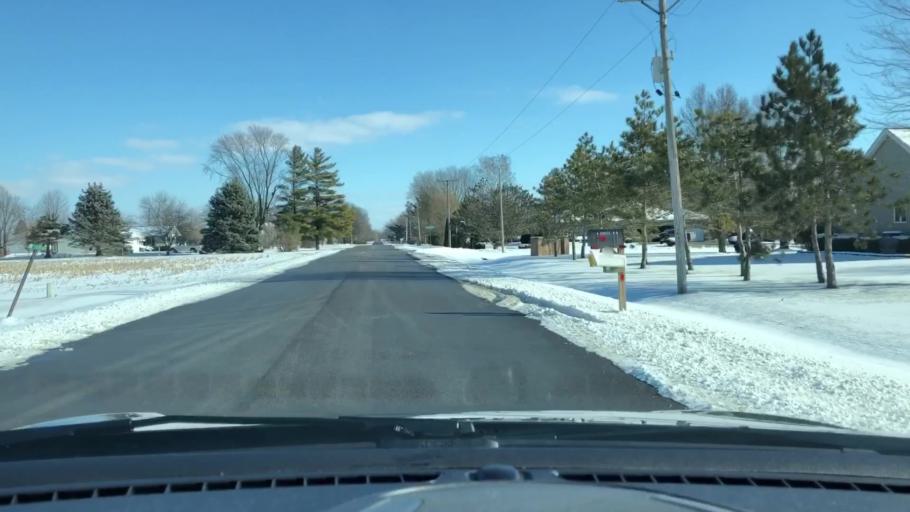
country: US
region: Illinois
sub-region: Will County
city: Elwood
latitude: 41.4369
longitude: -88.0905
